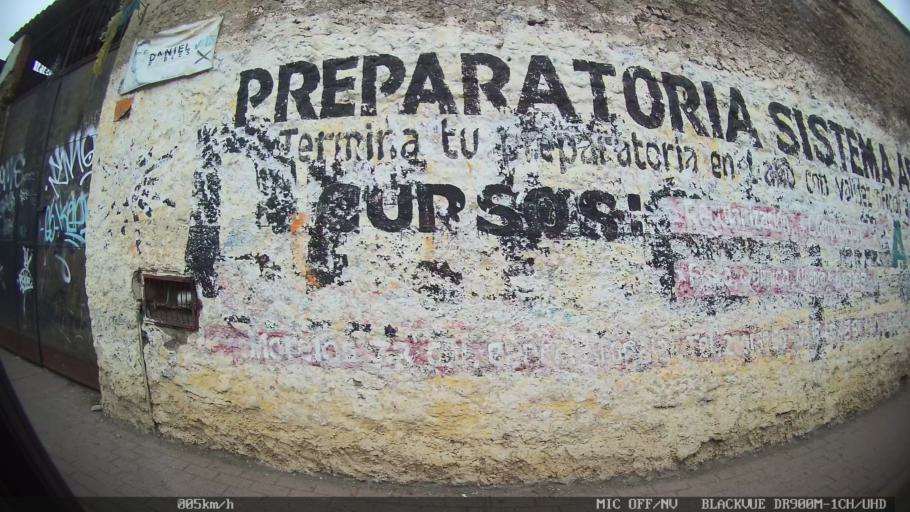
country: MX
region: Jalisco
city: Tonala
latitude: 20.6232
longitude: -103.2388
